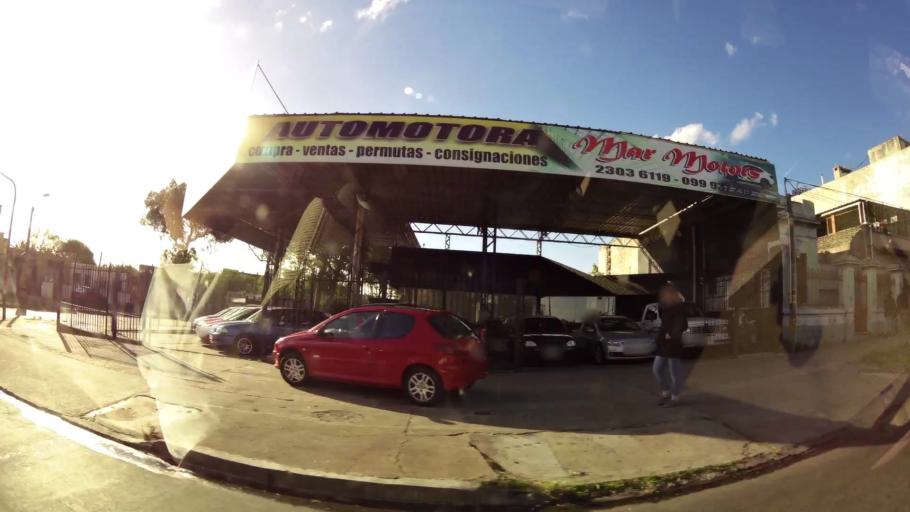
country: UY
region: Montevideo
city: Montevideo
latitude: -34.8694
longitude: -56.2403
